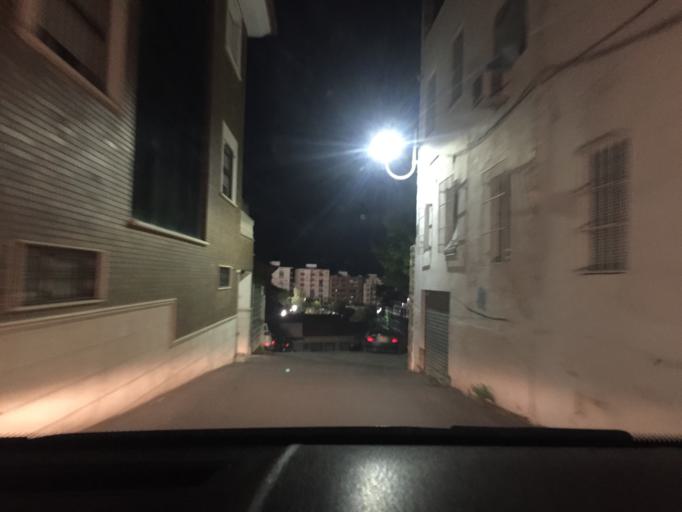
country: ES
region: Andalusia
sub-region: Provincia de Jaen
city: Jaen
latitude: 37.7667
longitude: -3.7820
